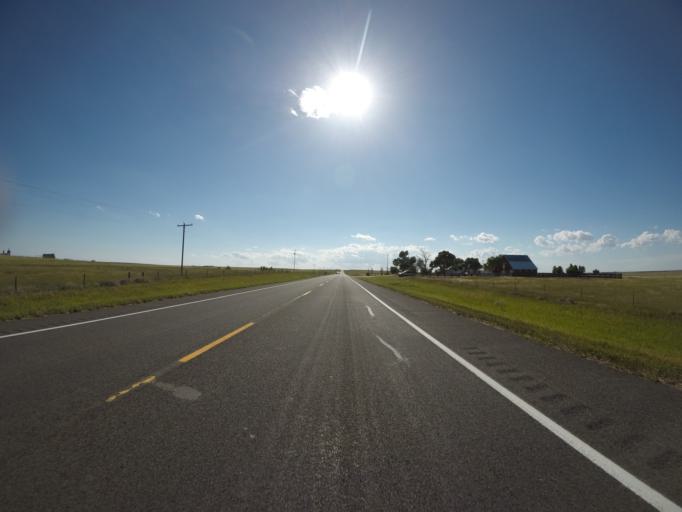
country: US
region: Colorado
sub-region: Morgan County
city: Brush
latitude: 40.6104
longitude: -103.6245
